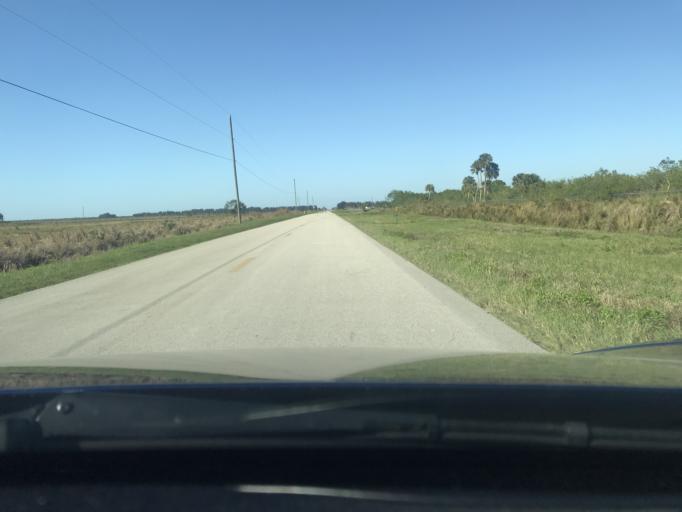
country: US
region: Florida
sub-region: Saint Lucie County
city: Fort Pierce South
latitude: 27.4076
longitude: -80.4975
